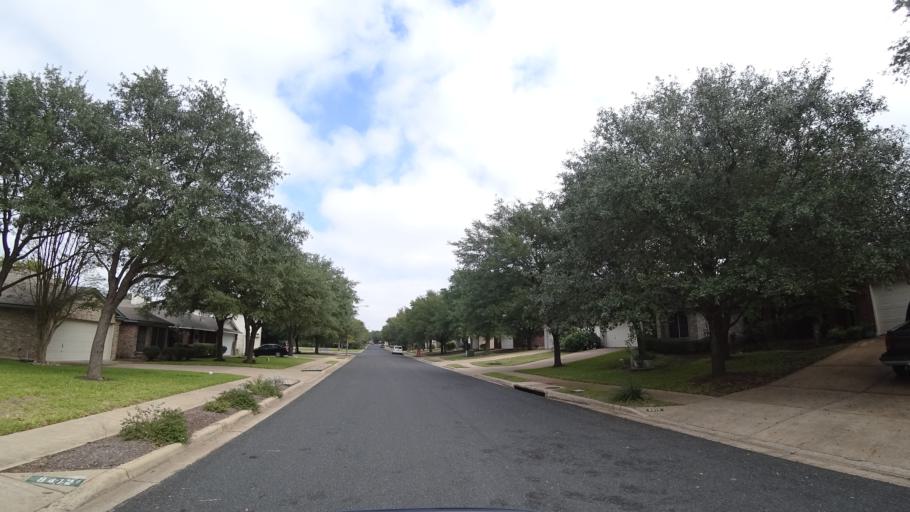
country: US
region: Texas
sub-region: Travis County
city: Shady Hollow
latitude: 30.1856
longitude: -97.8389
